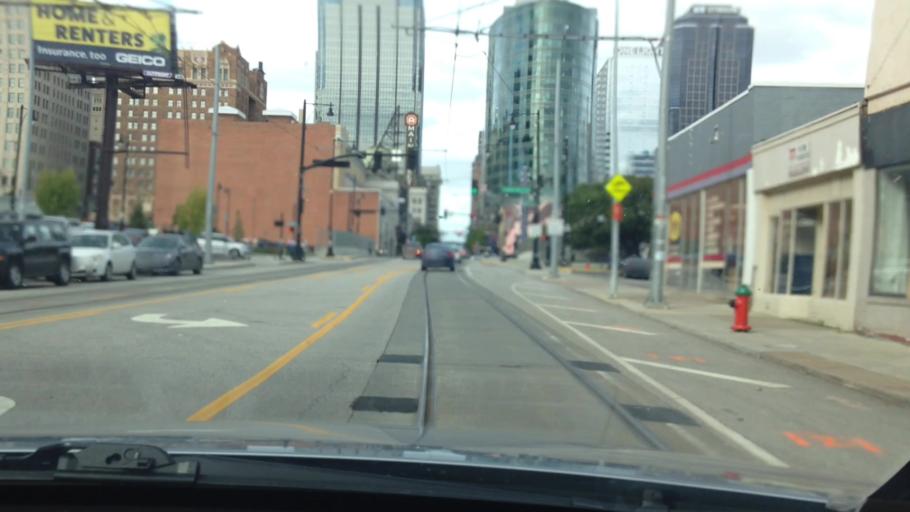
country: US
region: Missouri
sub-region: Jackson County
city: Kansas City
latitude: 39.0951
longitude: -94.5834
